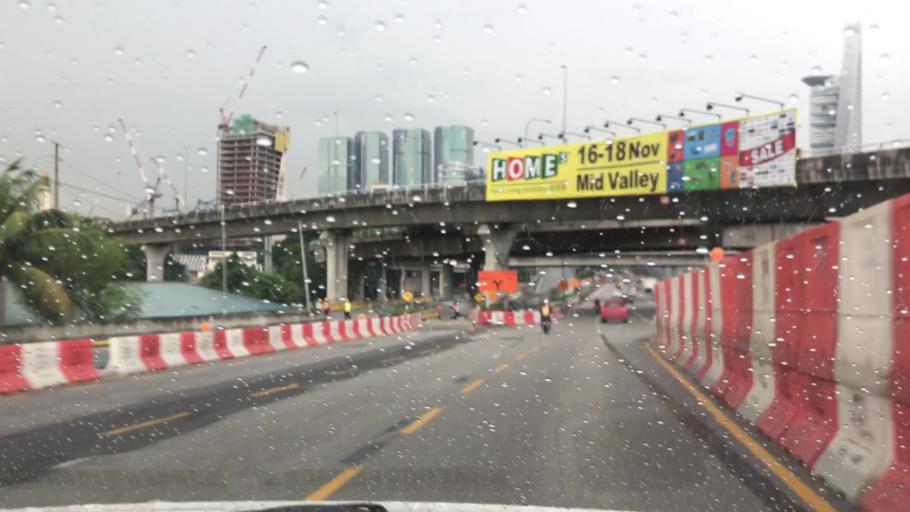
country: MY
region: Kuala Lumpur
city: Kuala Lumpur
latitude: 3.1148
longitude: 101.6761
